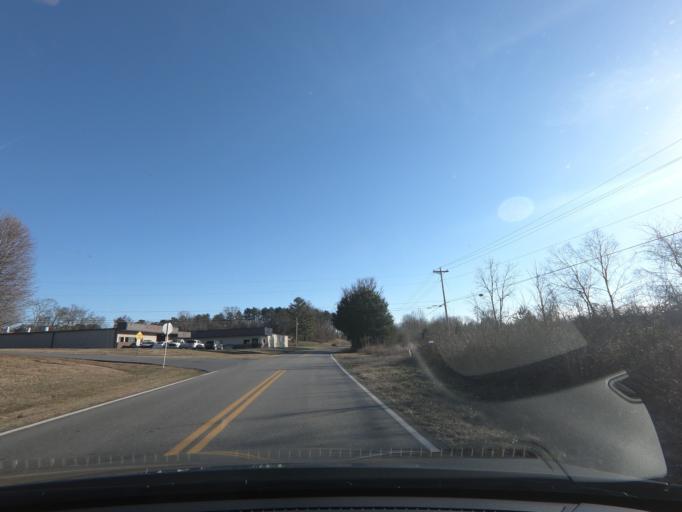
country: US
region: Georgia
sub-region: Gordon County
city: Calhoun
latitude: 34.4505
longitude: -84.9144
